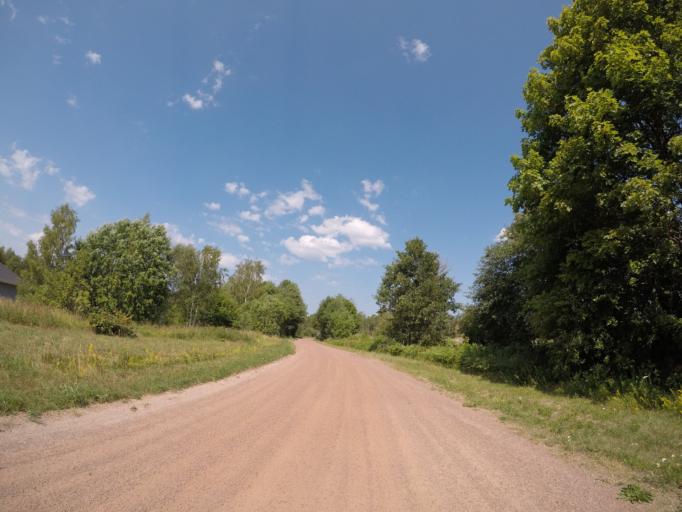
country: AX
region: Alands landsbygd
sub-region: Finstroem
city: Finstroem
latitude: 60.2156
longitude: 19.8558
